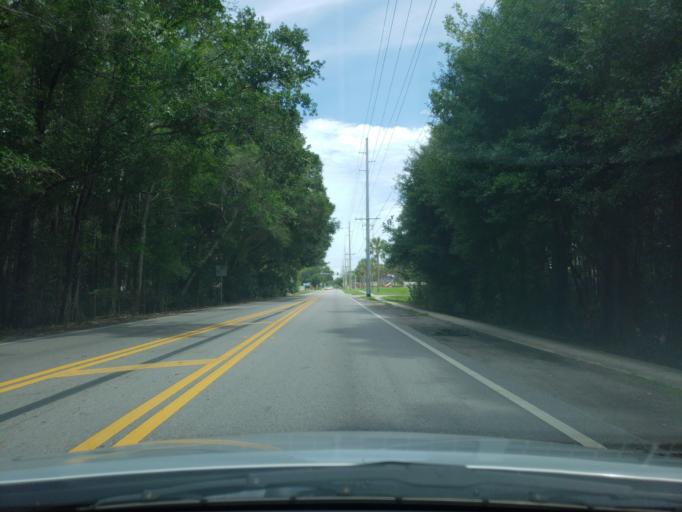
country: US
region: Florida
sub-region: Hillsborough County
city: Town 'n' Country
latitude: 28.0366
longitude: -82.5664
